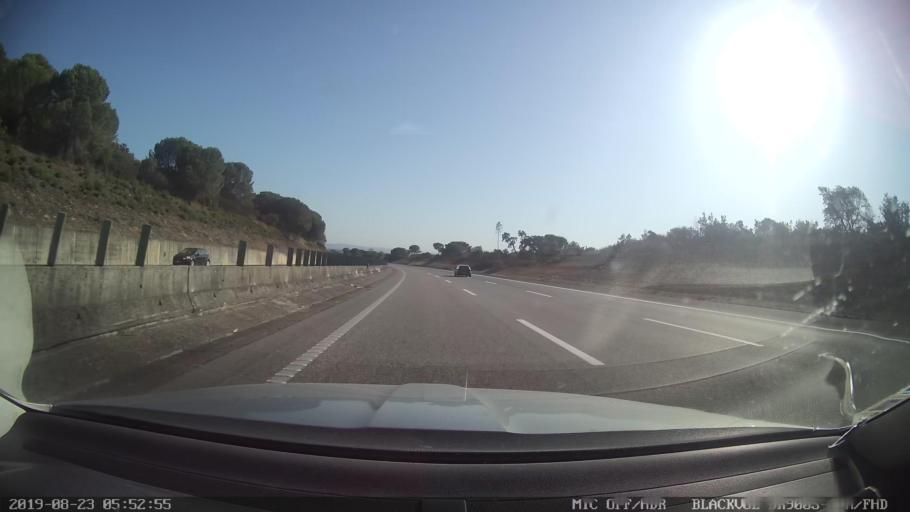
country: PT
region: Lisbon
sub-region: Azambuja
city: Aveiras de Cima
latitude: 39.1095
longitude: -8.9327
